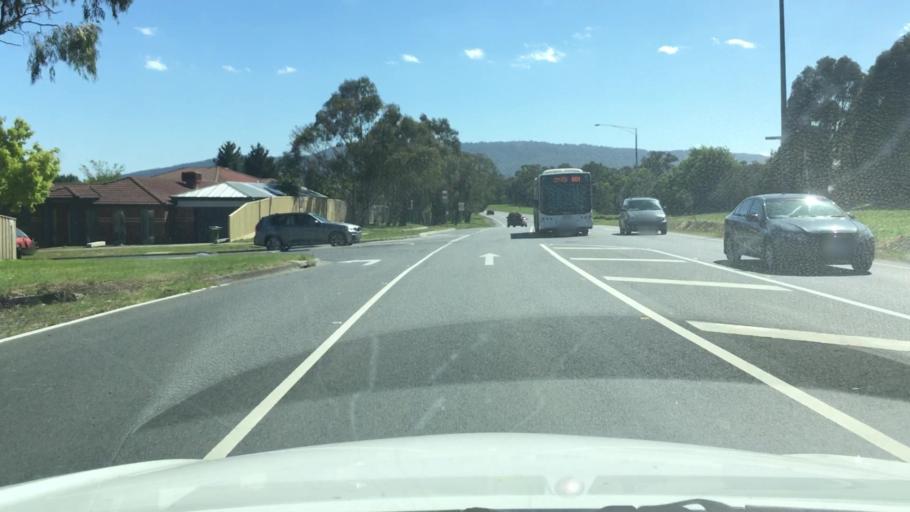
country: AU
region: Victoria
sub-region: Knox
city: Rowville
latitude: -37.9269
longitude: 145.2662
